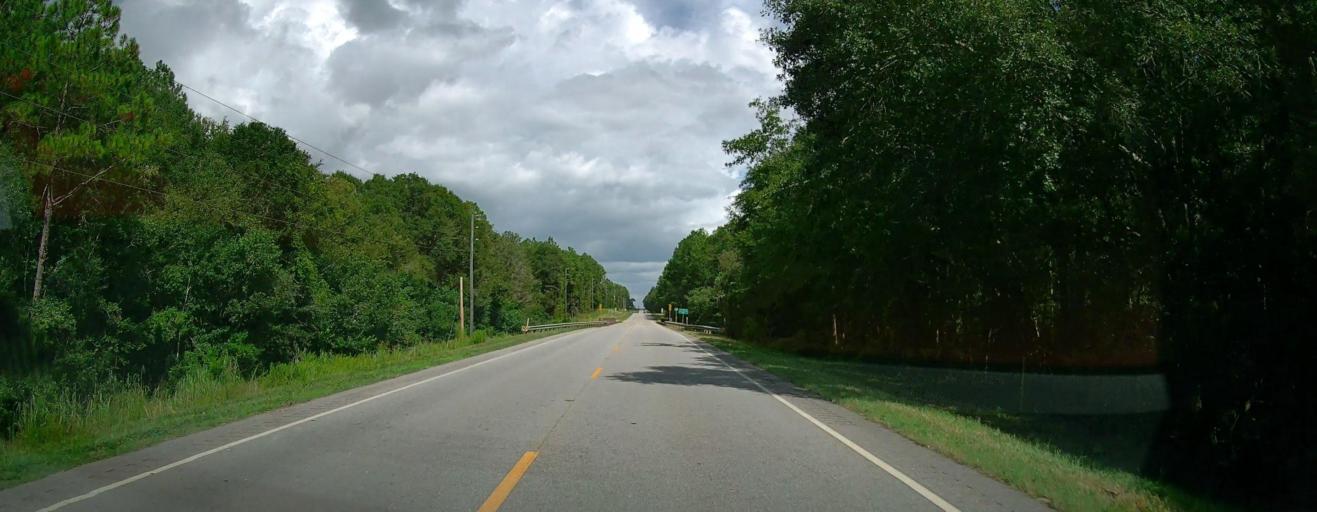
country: US
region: Georgia
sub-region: Coffee County
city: Broxton
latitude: 31.5752
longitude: -83.0413
